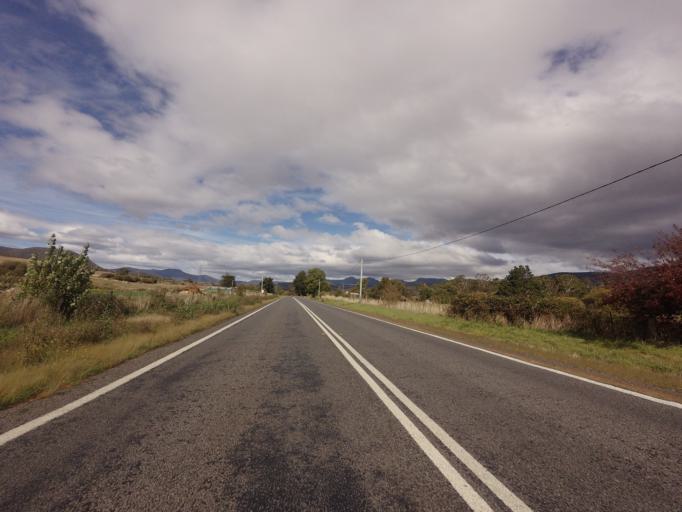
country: AU
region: Tasmania
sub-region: Derwent Valley
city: New Norfolk
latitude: -42.7617
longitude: 147.0125
